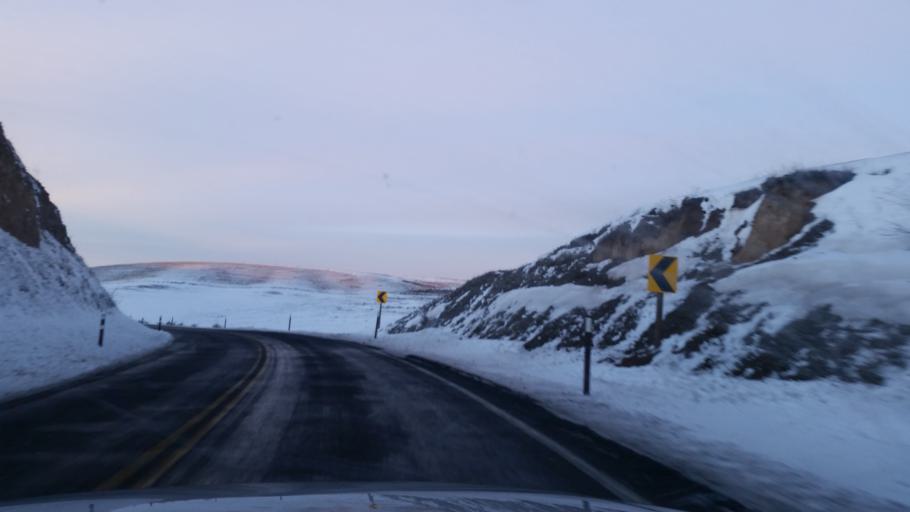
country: US
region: Washington
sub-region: Spokane County
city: Cheney
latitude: 47.1958
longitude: -117.8786
